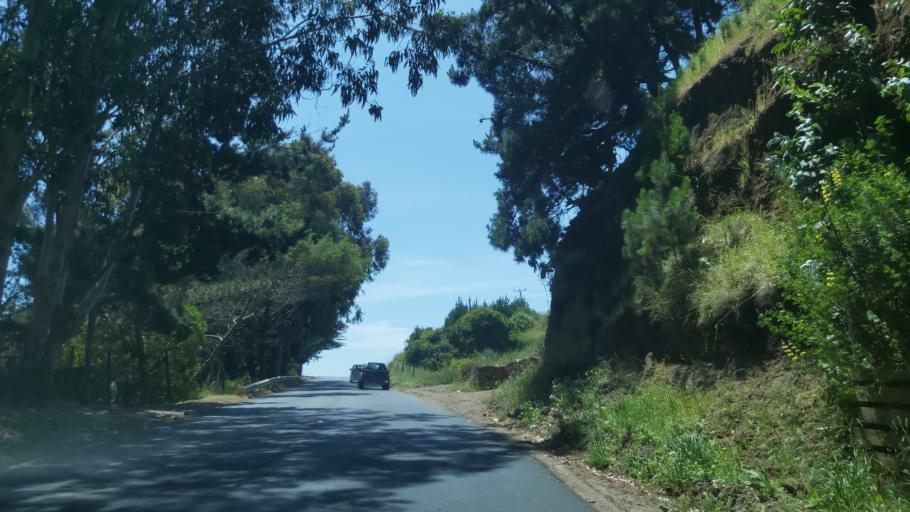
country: CL
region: Maule
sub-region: Provincia de Cauquenes
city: Cauquenes
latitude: -35.8284
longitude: -72.6149
